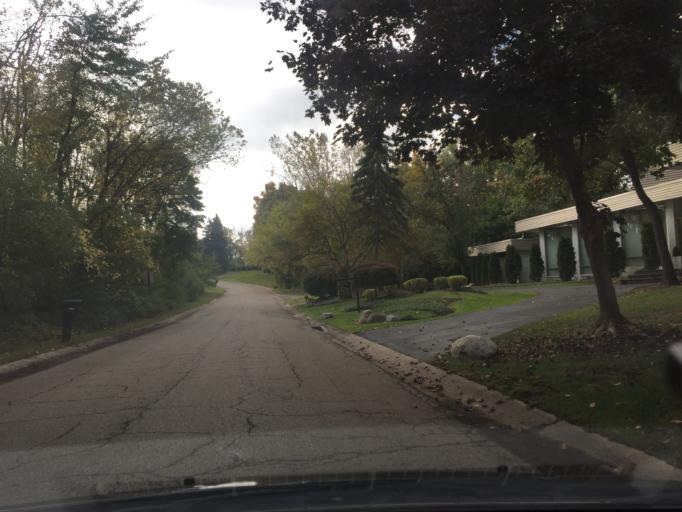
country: US
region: Michigan
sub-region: Oakland County
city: Sylvan Lake
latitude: 42.5905
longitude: -83.3183
